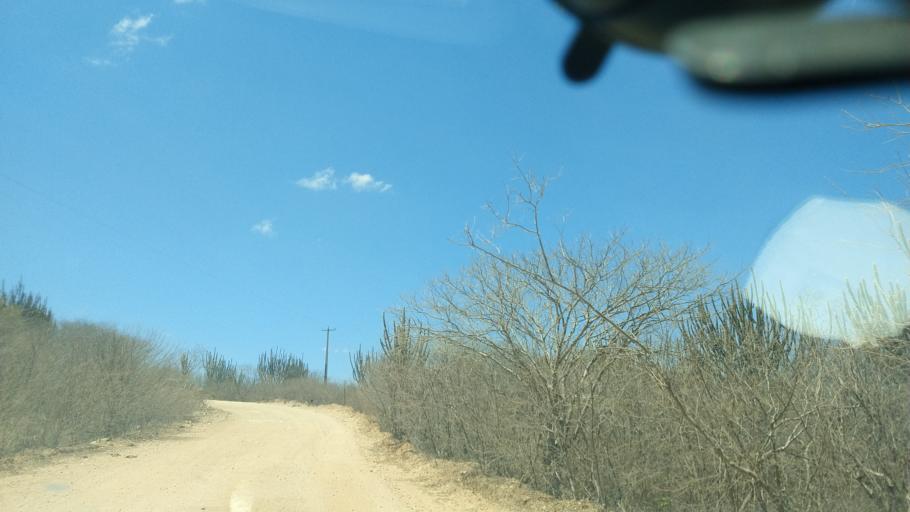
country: BR
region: Rio Grande do Norte
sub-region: Cerro Cora
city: Cerro Cora
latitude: -6.0099
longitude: -36.2800
